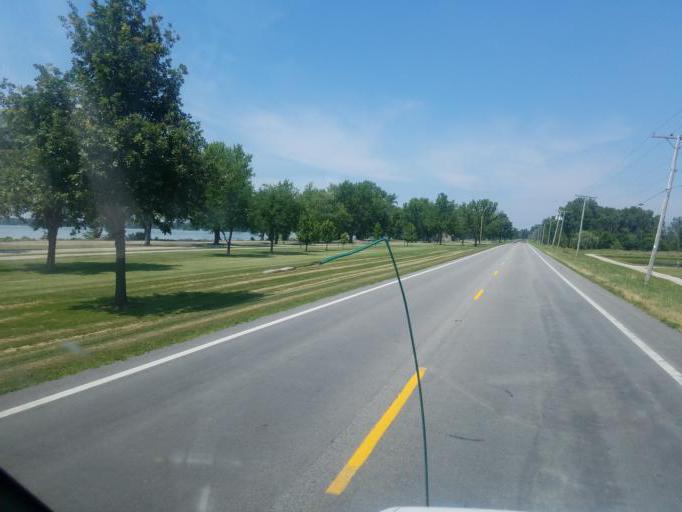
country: US
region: Ohio
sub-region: Auglaize County
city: Saint Marys
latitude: 40.5286
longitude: -84.4193
